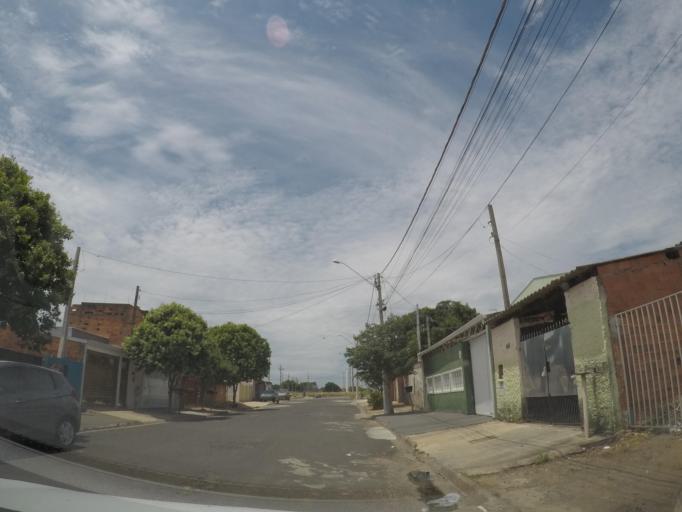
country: BR
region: Sao Paulo
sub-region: Hortolandia
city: Hortolandia
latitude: -22.8391
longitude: -47.1954
